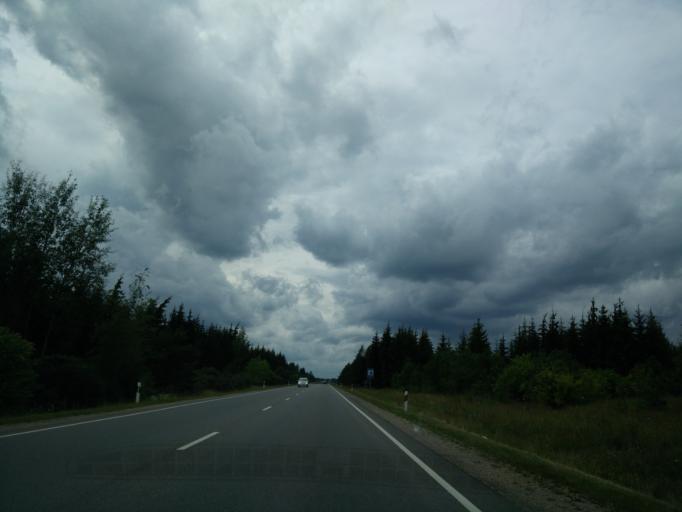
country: LT
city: Trakai
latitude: 54.6258
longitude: 24.9844
